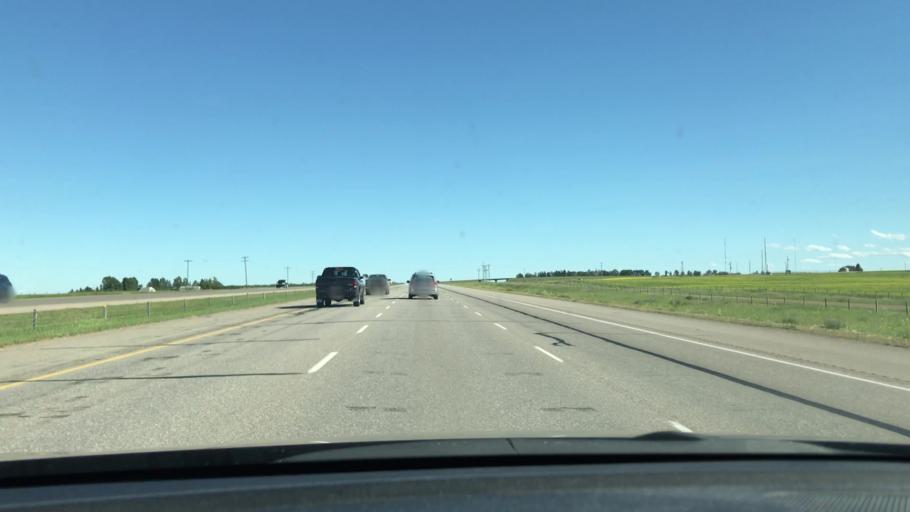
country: CA
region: Alberta
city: Crossfield
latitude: 51.4448
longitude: -114.0108
